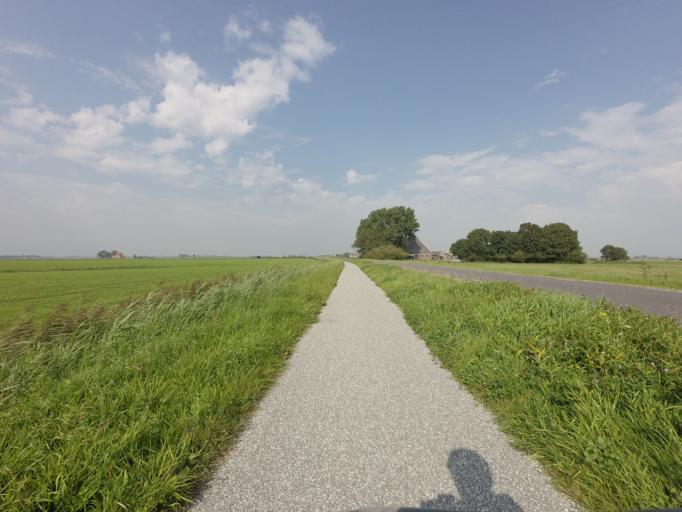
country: NL
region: Friesland
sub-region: Sudwest Fryslan
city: Bolsward
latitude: 53.0252
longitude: 5.5372
